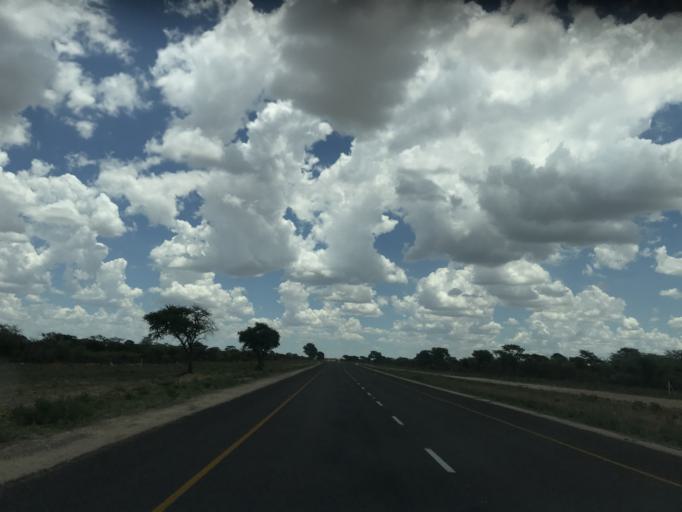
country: BW
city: Mabuli
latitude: -25.8026
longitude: 24.8426
